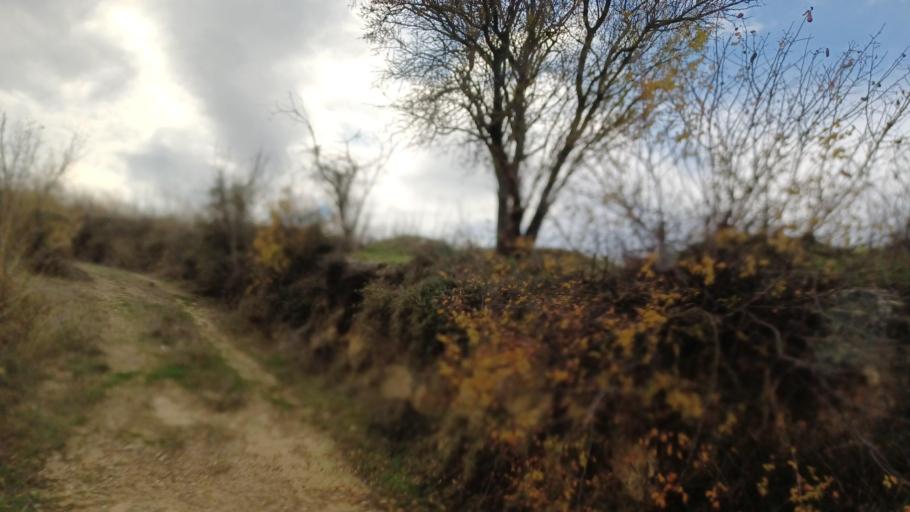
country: CY
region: Limassol
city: Pachna
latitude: 34.7814
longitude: 32.8154
